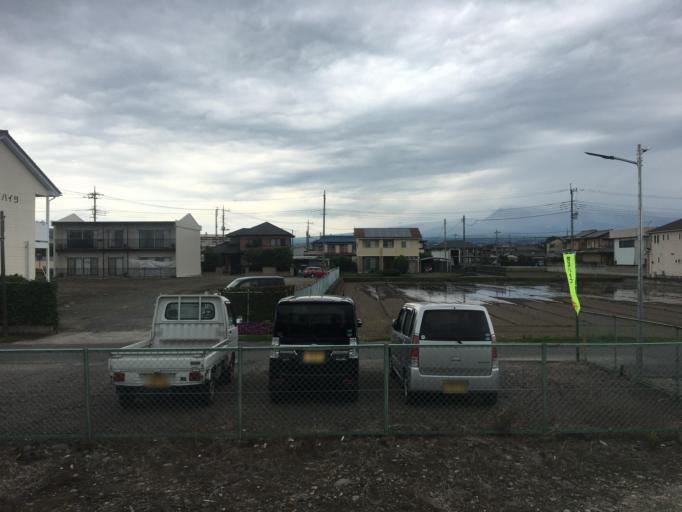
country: JP
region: Gunma
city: Maebashi-shi
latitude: 36.3943
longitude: 139.1057
